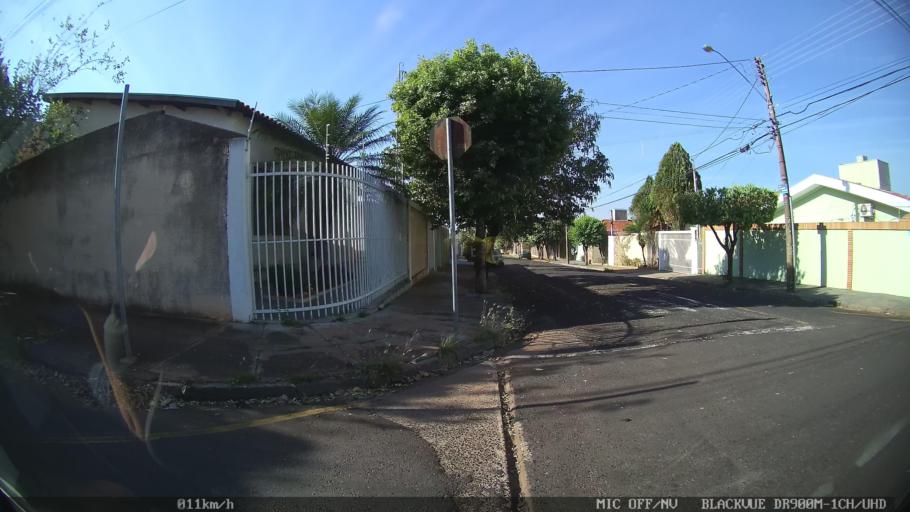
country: BR
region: Sao Paulo
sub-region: Sao Jose Do Rio Preto
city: Sao Jose do Rio Preto
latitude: -20.7853
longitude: -49.3565
